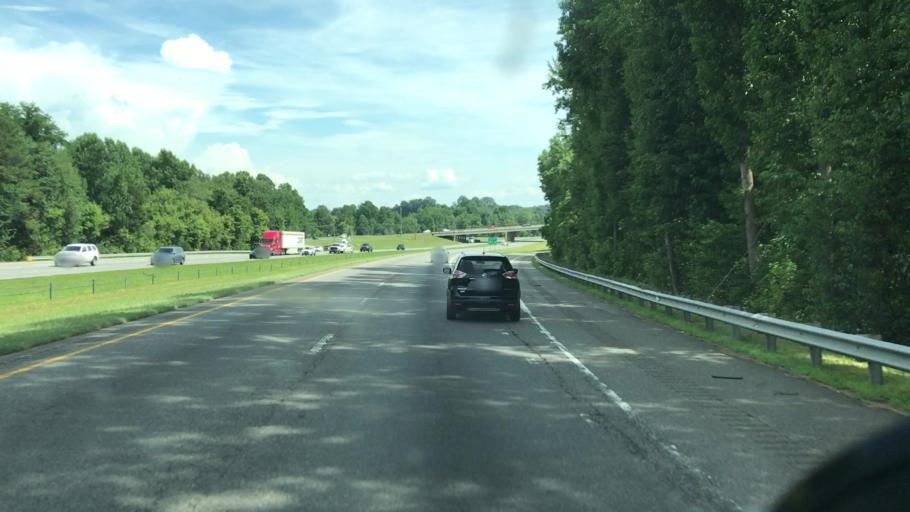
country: US
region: North Carolina
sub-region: Iredell County
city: Statesville
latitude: 35.8532
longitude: -80.8604
